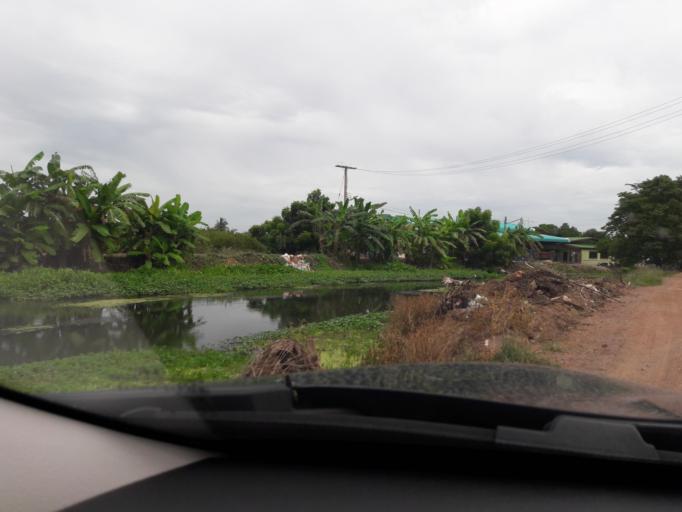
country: TH
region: Ratchaburi
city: Bang Phae
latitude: 13.6275
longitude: 99.9629
